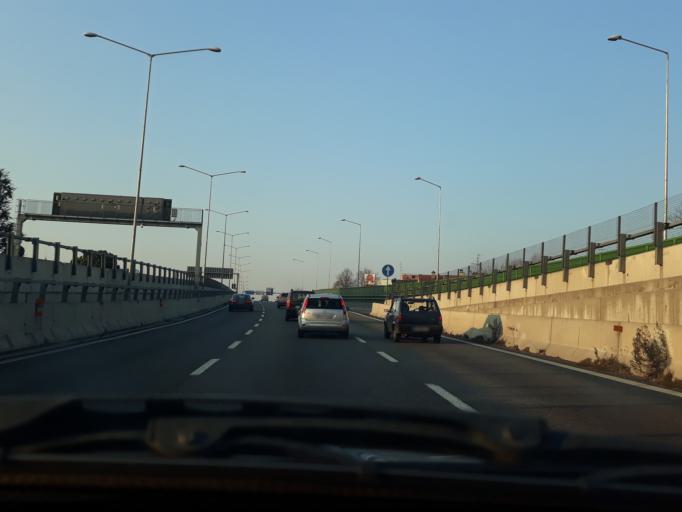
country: IT
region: Lombardy
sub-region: Provincia di Monza e Brianza
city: Muggio
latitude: 45.5856
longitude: 9.2504
